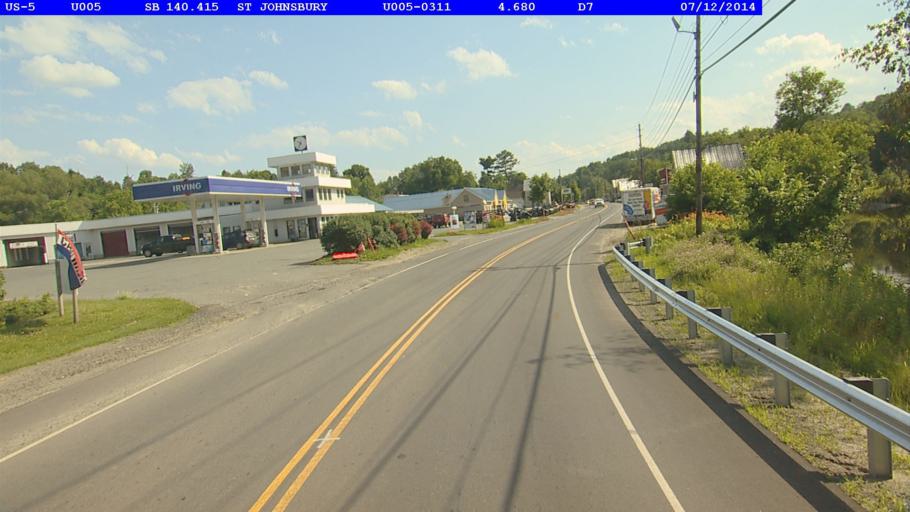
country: US
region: Vermont
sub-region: Caledonia County
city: St Johnsbury
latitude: 44.4586
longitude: -72.0152
